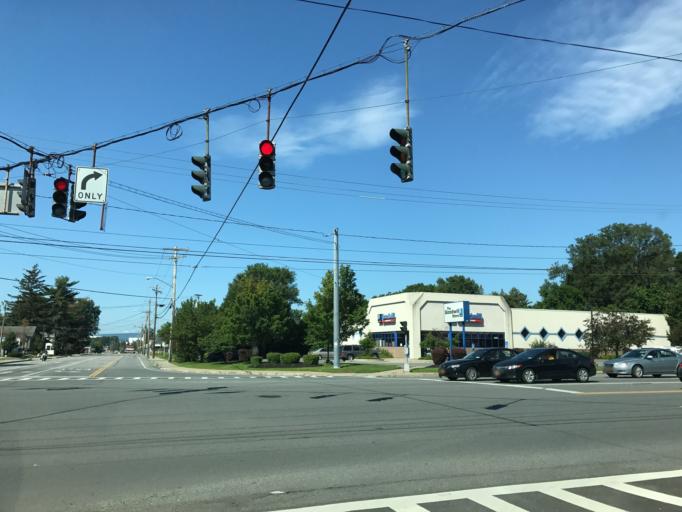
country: US
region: New York
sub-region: Albany County
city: Roessleville
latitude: 42.7034
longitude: -73.8163
